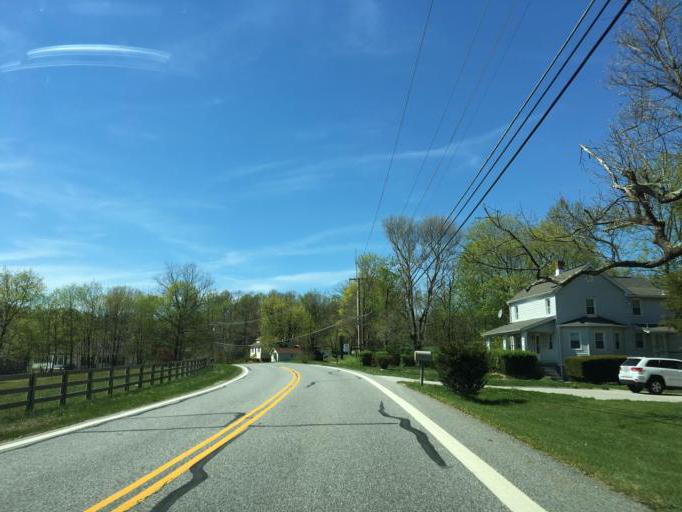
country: US
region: Maryland
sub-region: Baltimore County
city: Hunt Valley
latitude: 39.5910
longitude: -76.6384
